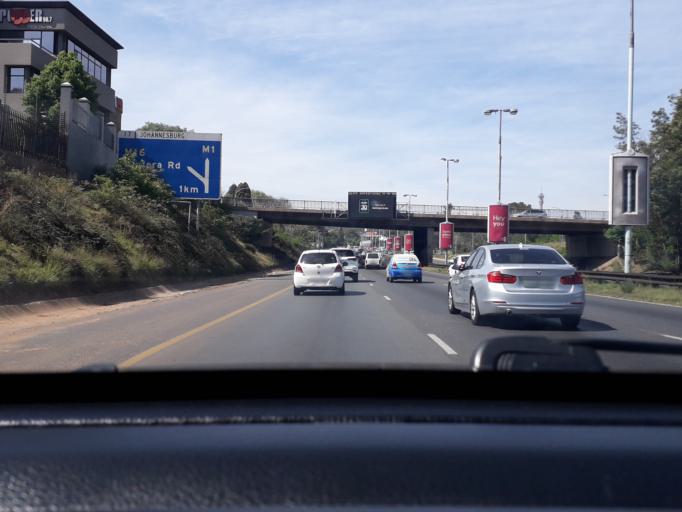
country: ZA
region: Gauteng
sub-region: City of Johannesburg Metropolitan Municipality
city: Johannesburg
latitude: -26.1547
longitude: 28.0574
